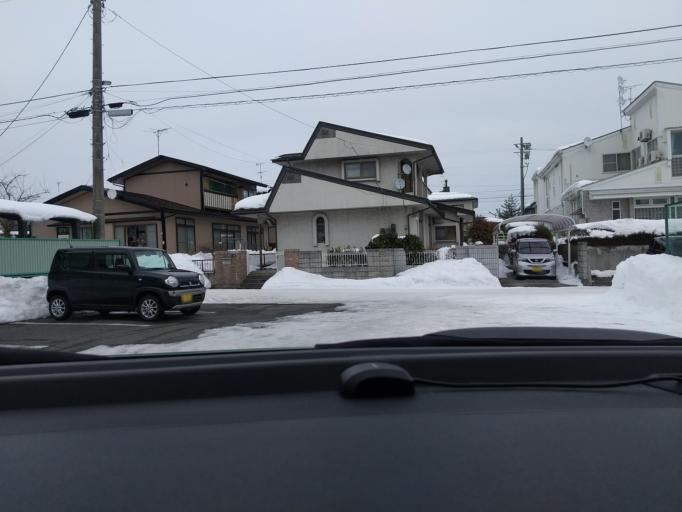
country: JP
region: Iwate
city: Morioka-shi
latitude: 39.7348
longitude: 141.0875
